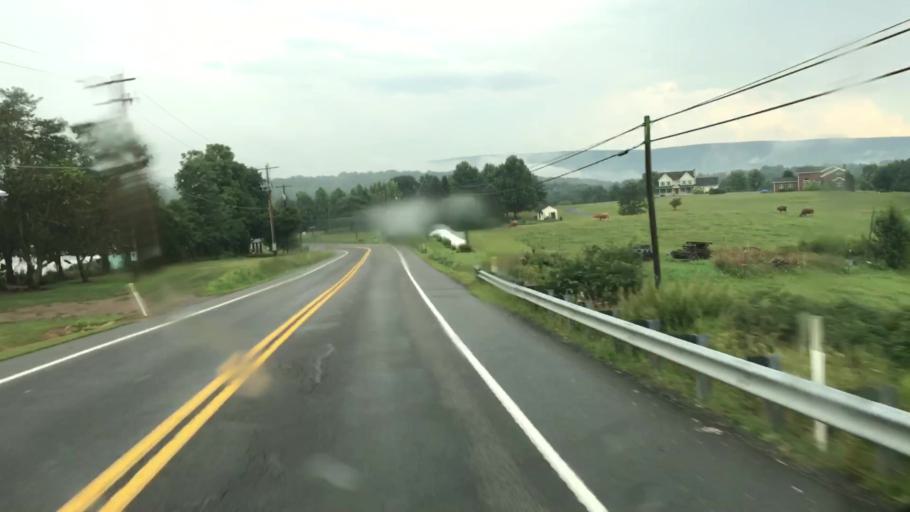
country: US
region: Pennsylvania
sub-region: Perry County
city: Duncannon
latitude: 40.4067
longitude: -77.0910
